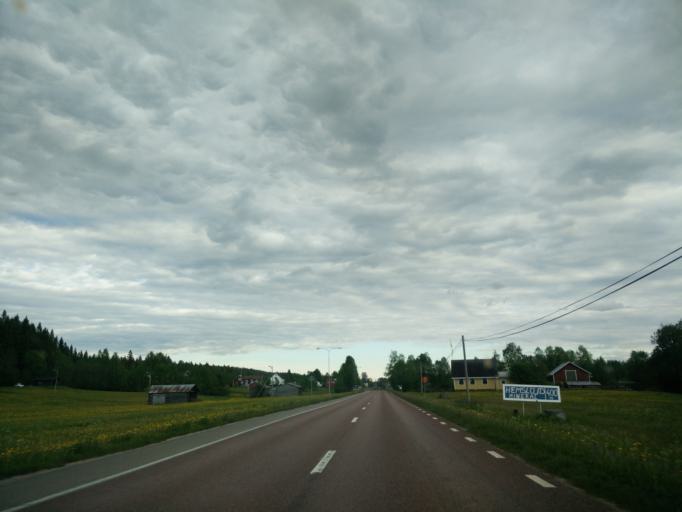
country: SE
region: Jaemtland
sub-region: Harjedalens Kommun
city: Sveg
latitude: 62.2851
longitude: 14.7984
